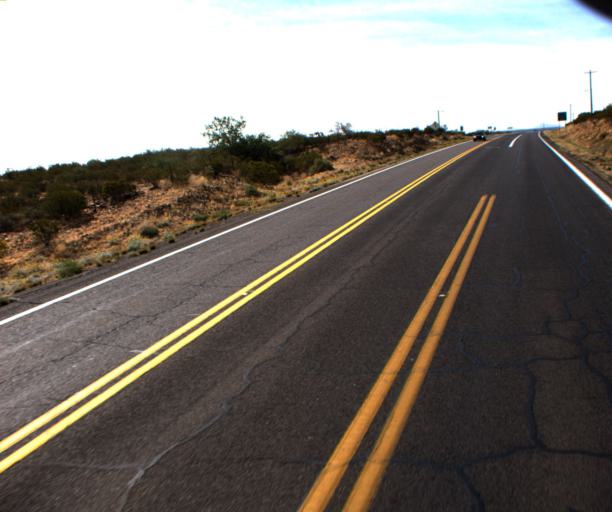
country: US
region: Arizona
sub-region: Graham County
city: Swift Trail Junction
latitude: 32.7167
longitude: -109.7088
